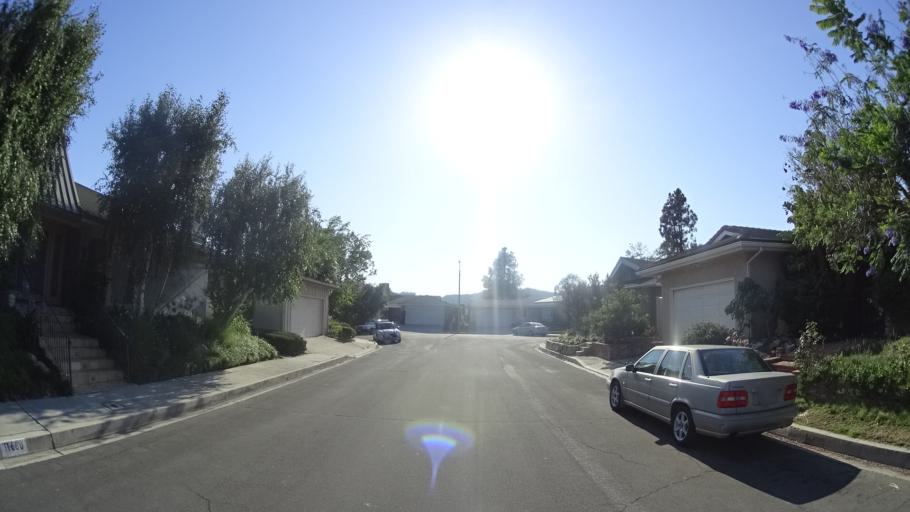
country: US
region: California
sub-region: Los Angeles County
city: Universal City
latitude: 34.1306
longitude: -118.3883
